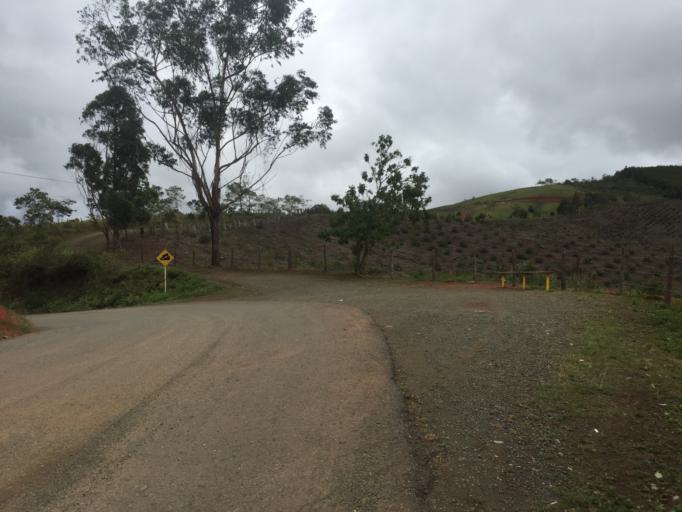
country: CO
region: Valle del Cauca
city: Dagua
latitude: 3.7097
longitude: -76.5859
